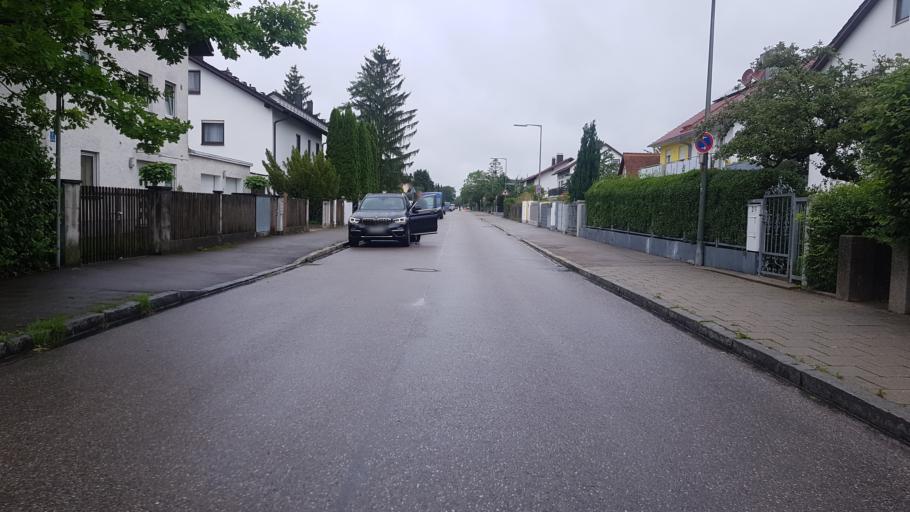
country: DE
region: Bavaria
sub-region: Upper Bavaria
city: Unterfoehring
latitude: 48.2056
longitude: 11.5995
